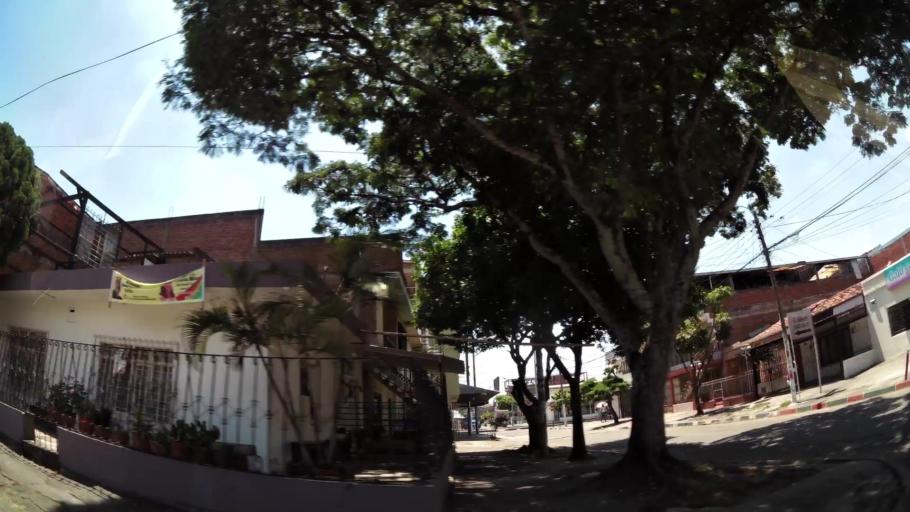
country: CO
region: Valle del Cauca
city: Cali
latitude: 3.4335
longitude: -76.5078
